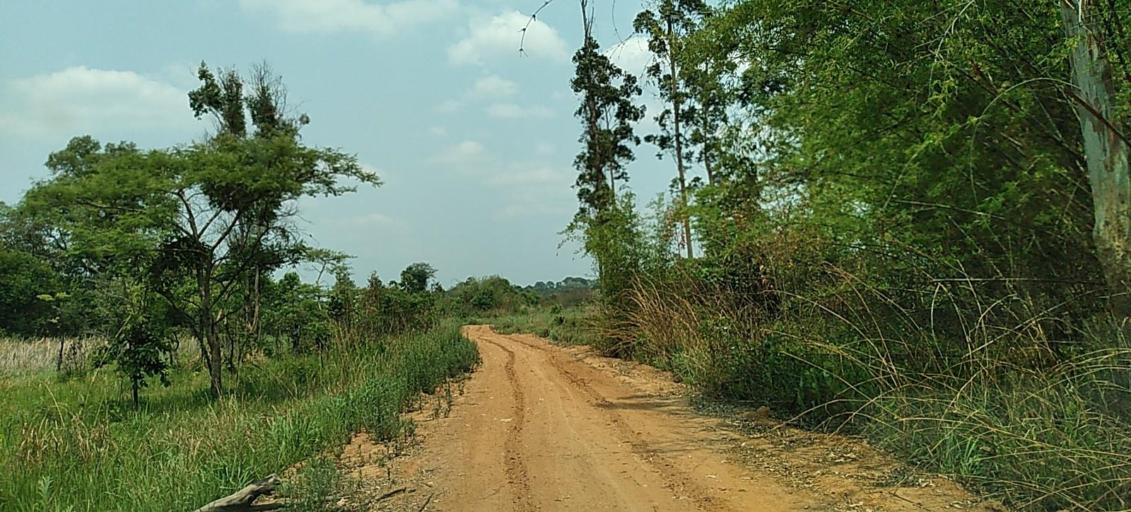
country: ZM
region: Copperbelt
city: Kalulushi
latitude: -12.7585
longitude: 28.0254
